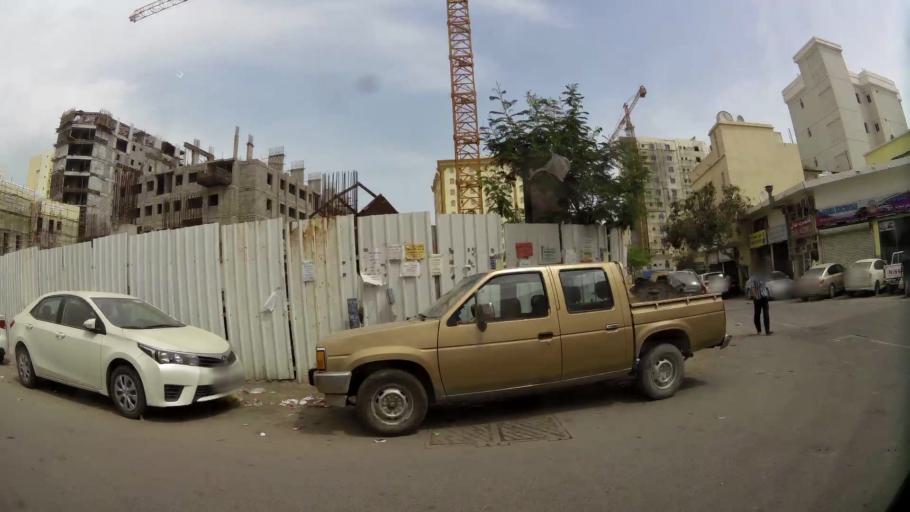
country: QA
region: Baladiyat ad Dawhah
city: Doha
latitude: 25.2766
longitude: 51.5231
